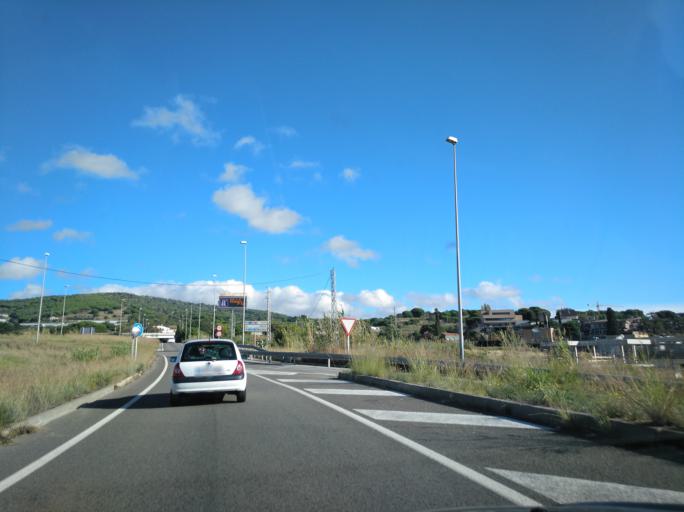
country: ES
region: Catalonia
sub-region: Provincia de Barcelona
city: Mataro
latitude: 41.5540
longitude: 2.4575
